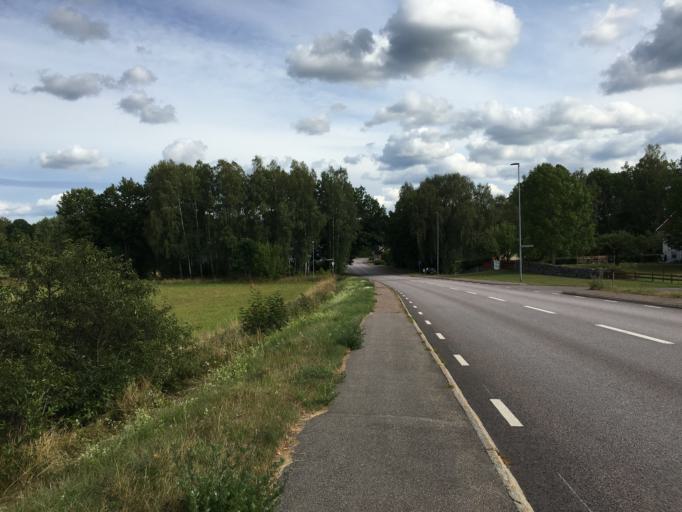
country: SE
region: Kalmar
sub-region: Nybro Kommun
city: Nybro
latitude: 56.9457
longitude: 15.9117
